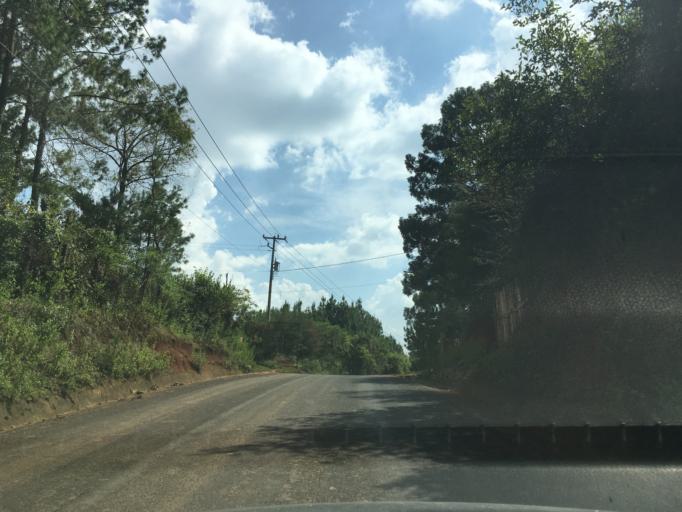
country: MX
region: Michoacan
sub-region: Morelia
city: Morelos
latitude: 19.5631
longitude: -101.1932
